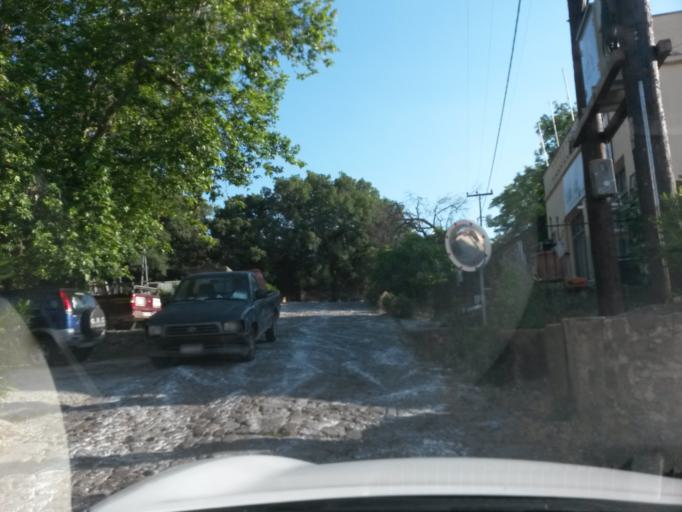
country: GR
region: North Aegean
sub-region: Nomos Lesvou
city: Mantamados
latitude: 39.3455
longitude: 26.3211
